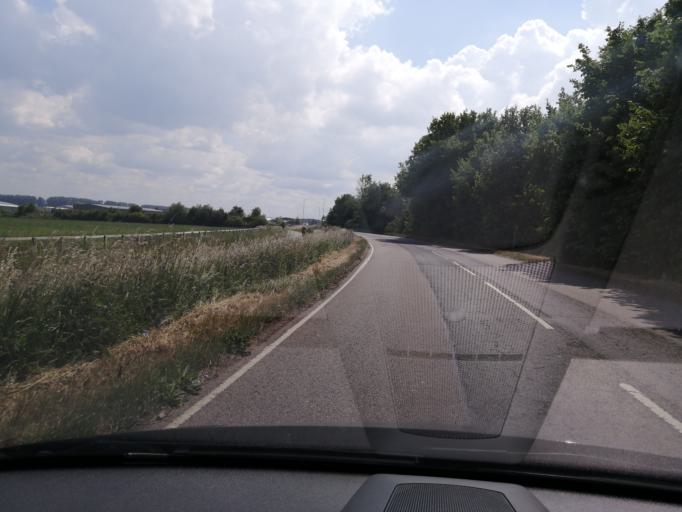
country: GB
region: England
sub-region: Cambridgeshire
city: Yaxley
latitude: 52.5296
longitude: -0.2379
